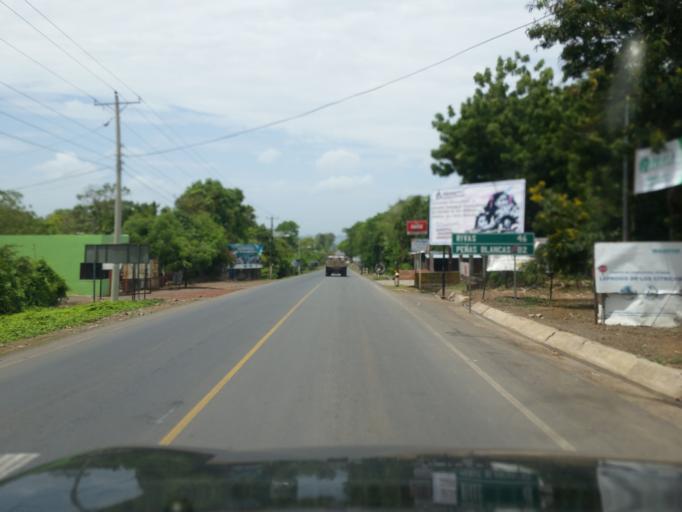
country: NI
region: Granada
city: Nandaime
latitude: 11.7760
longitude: -86.0530
